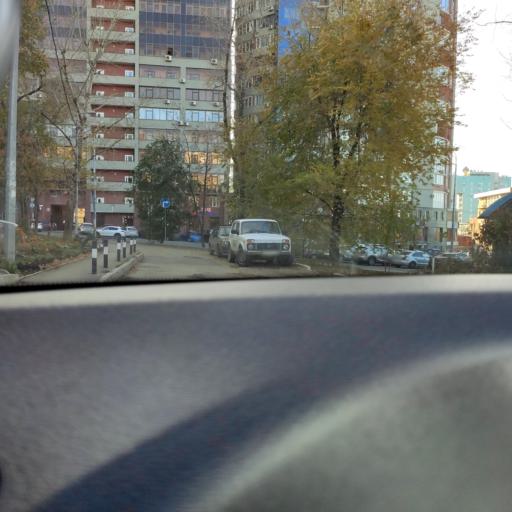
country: RU
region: Samara
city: Samara
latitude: 53.2126
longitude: 50.1301
